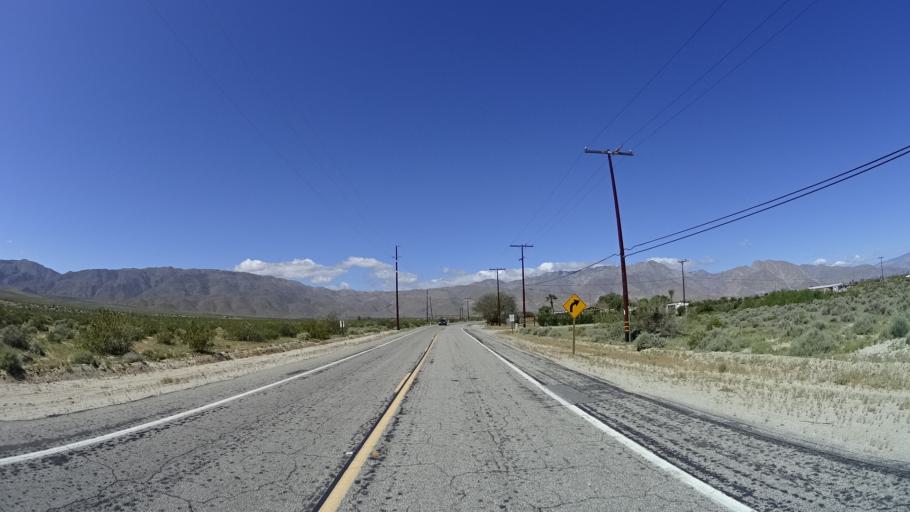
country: US
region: California
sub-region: San Diego County
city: Borrego Springs
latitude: 33.2208
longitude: -116.3434
